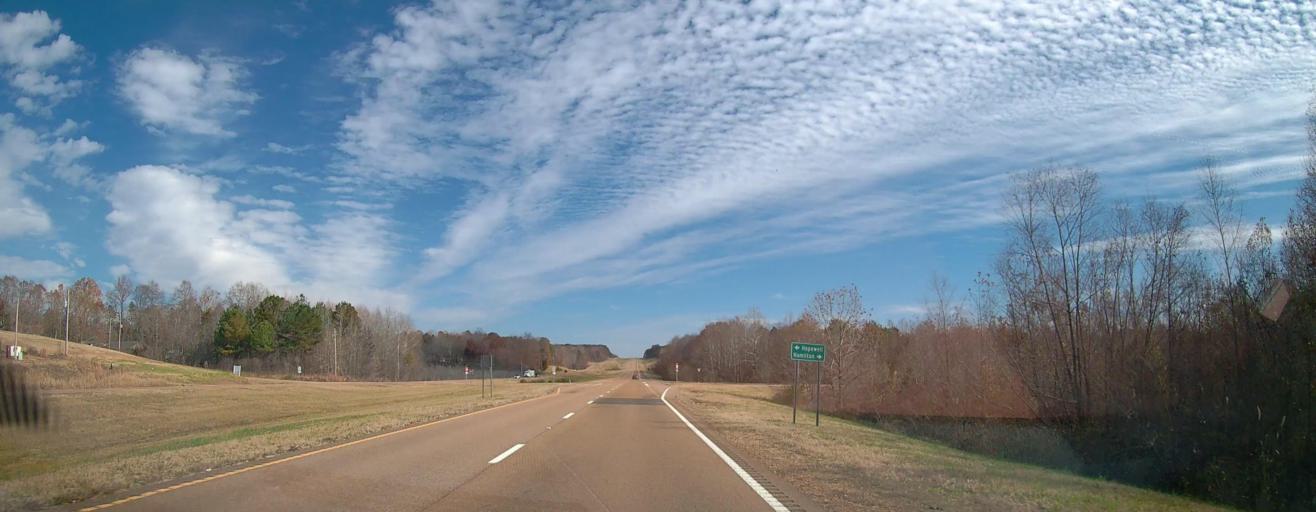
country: US
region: Mississippi
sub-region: Benton County
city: Ashland
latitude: 34.9519
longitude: -89.0605
